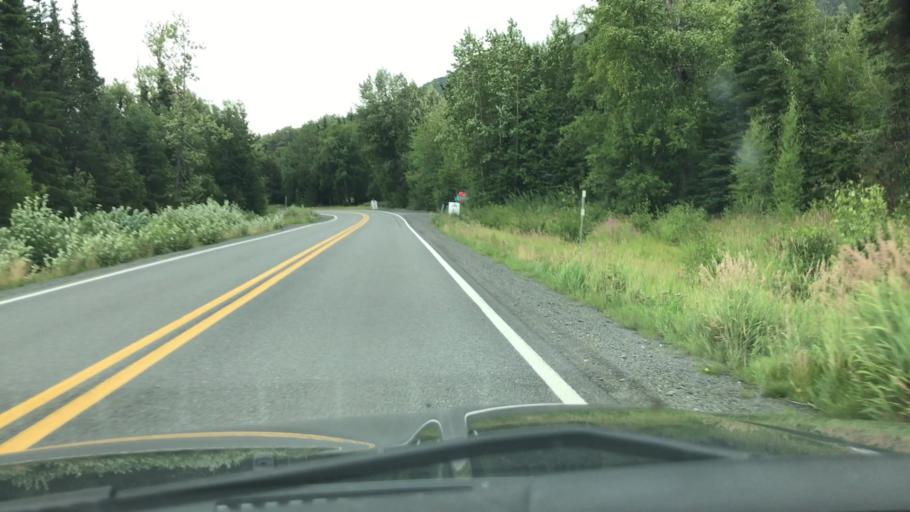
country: US
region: Alaska
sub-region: Kenai Peninsula Borough
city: Seward
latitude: 60.4879
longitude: -149.9761
